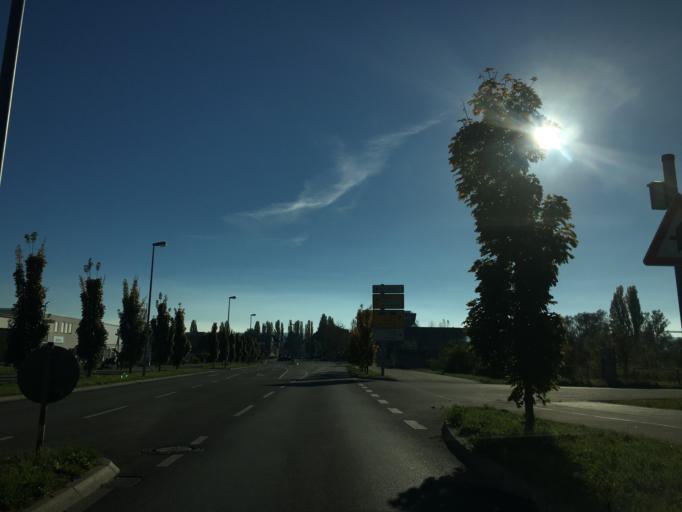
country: CH
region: Thurgau
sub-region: Kreuzlingen District
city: Gottlieben
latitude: 47.6798
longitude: 9.1466
